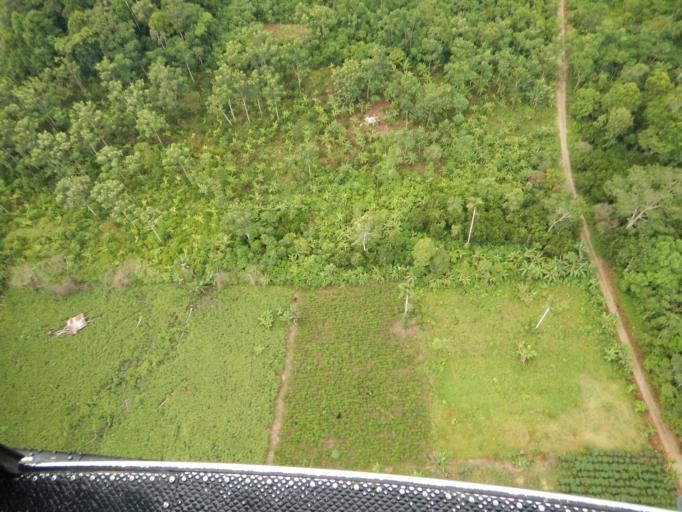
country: BO
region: Cochabamba
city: Chimore
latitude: -16.9665
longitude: -65.0772
